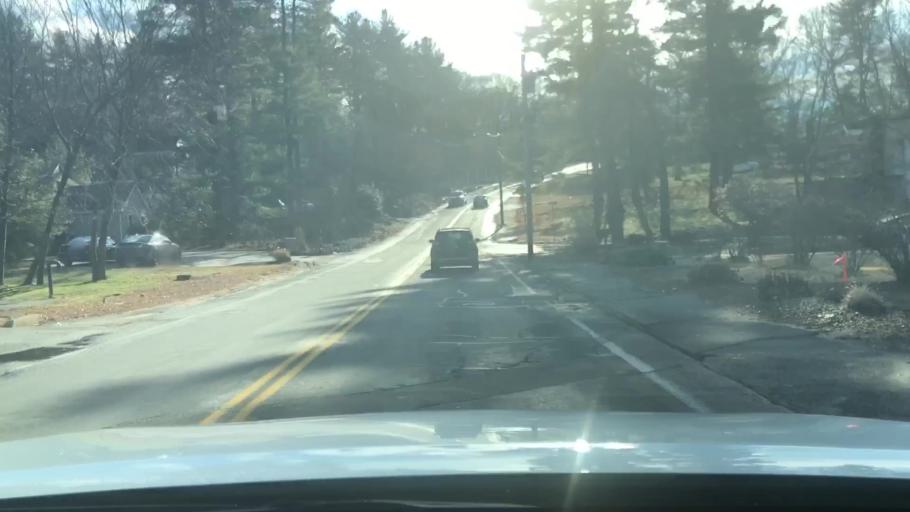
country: US
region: Rhode Island
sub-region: Providence County
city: Woonsocket
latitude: 42.0219
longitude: -71.4862
